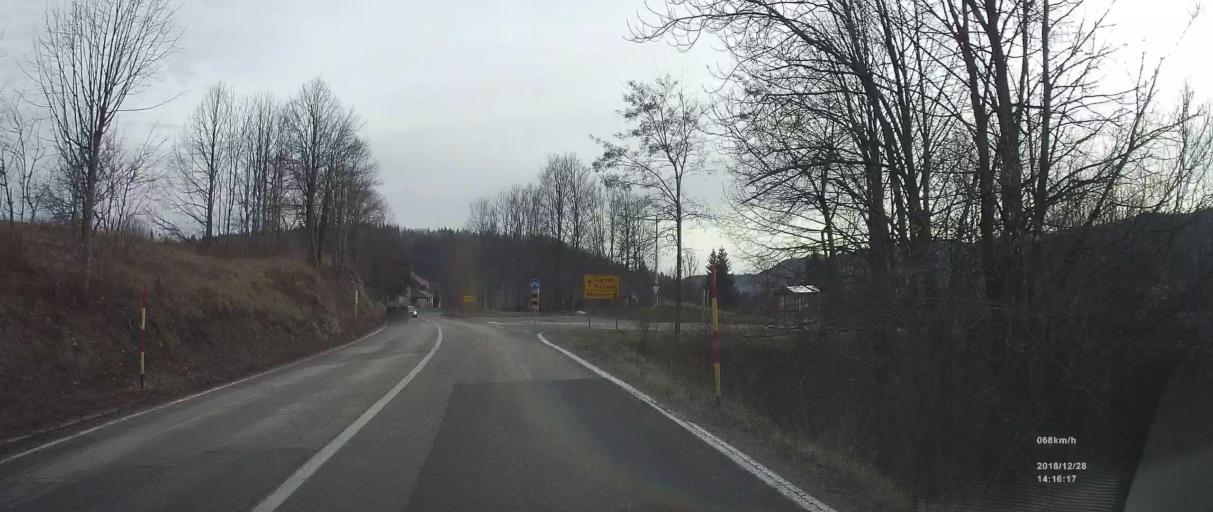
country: HR
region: Primorsko-Goranska
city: Vrbovsko
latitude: 45.4198
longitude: 15.0347
